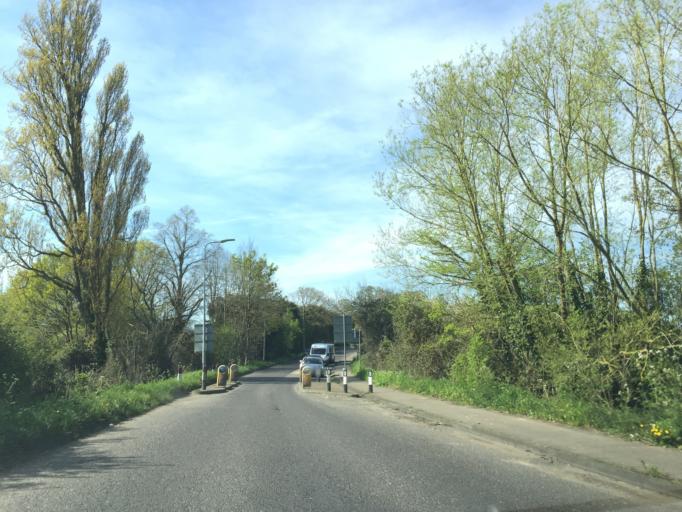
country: GB
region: England
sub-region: Greater London
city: Collier Row
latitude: 51.6245
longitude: 0.1895
